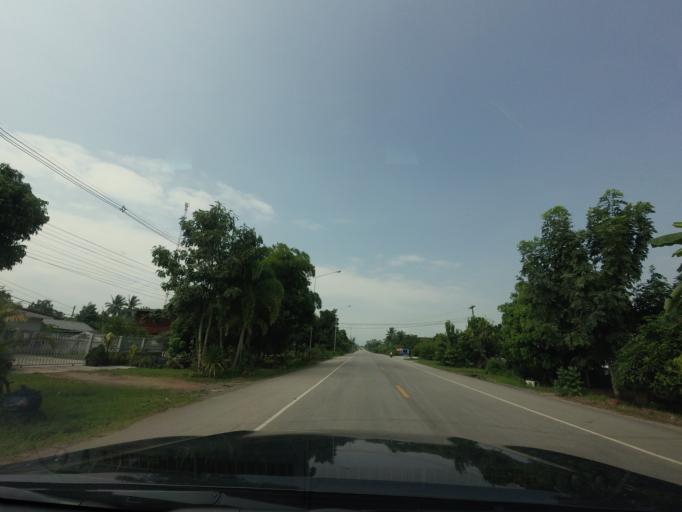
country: LA
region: Xiagnabouli
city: Muang Kenthao
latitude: 17.7067
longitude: 101.4205
